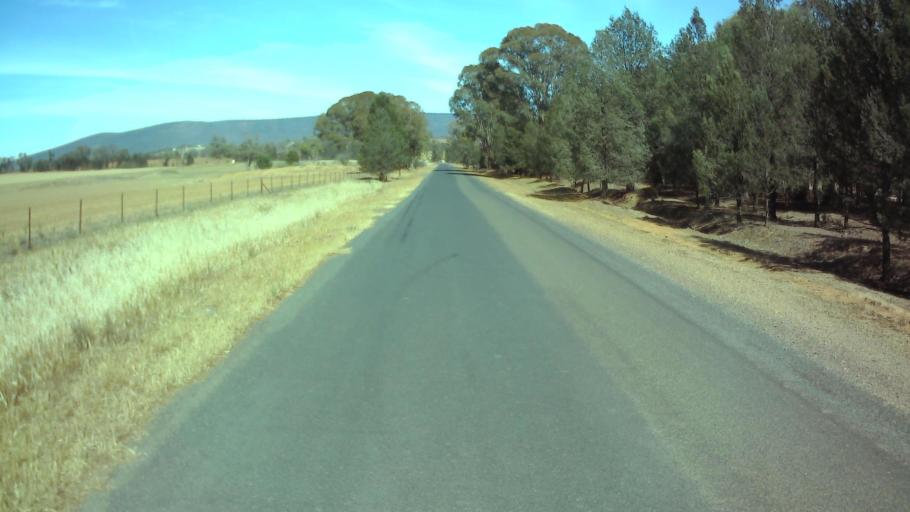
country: AU
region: New South Wales
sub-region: Weddin
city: Grenfell
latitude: -33.9316
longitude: 148.0911
